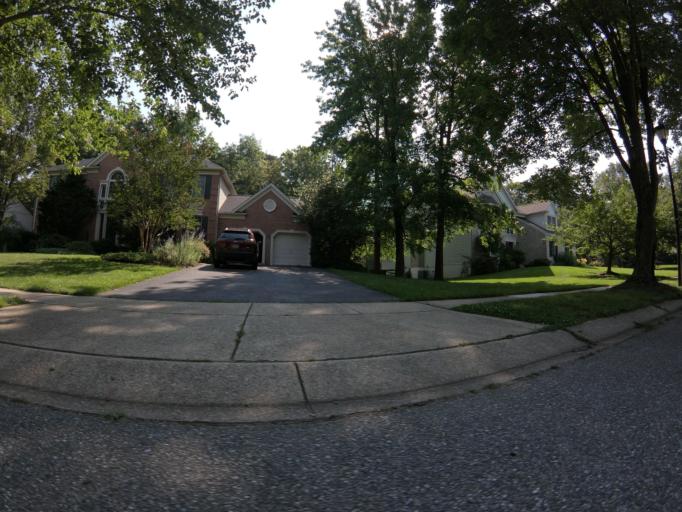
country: US
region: Maryland
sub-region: Anne Arundel County
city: Pasadena
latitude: 39.0979
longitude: -76.5729
